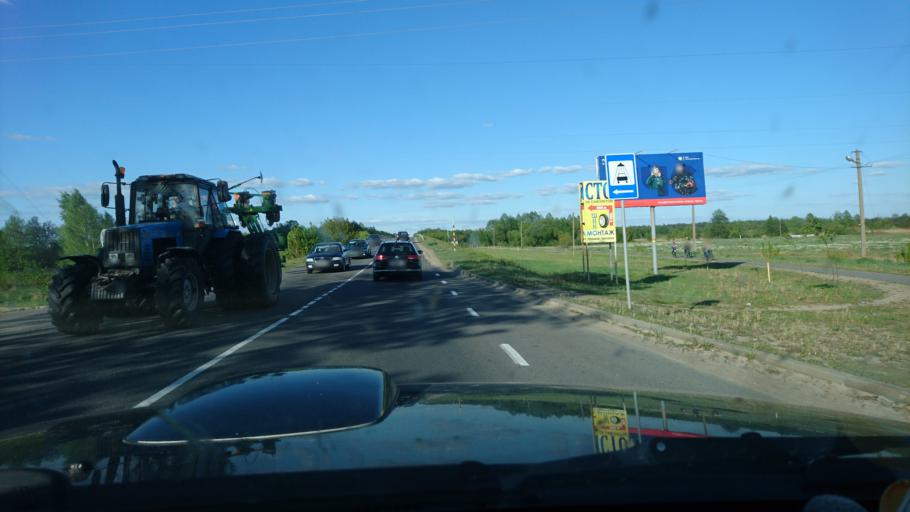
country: BY
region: Brest
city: Byaroza
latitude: 52.5403
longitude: 24.9968
